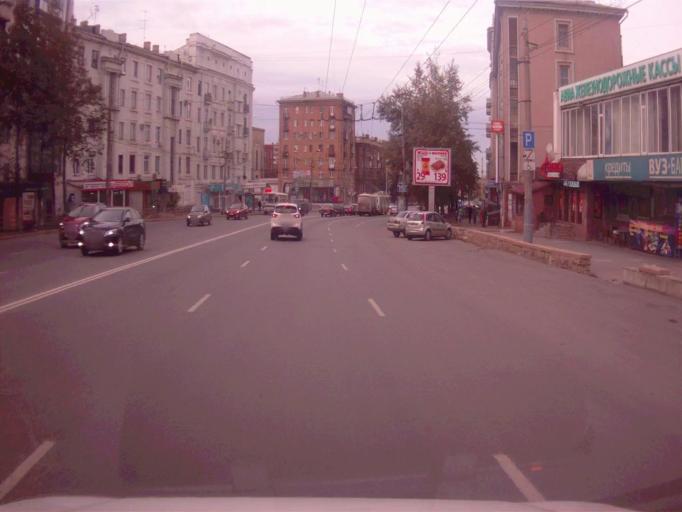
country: RU
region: Chelyabinsk
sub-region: Gorod Chelyabinsk
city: Chelyabinsk
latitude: 55.1595
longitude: 61.4116
